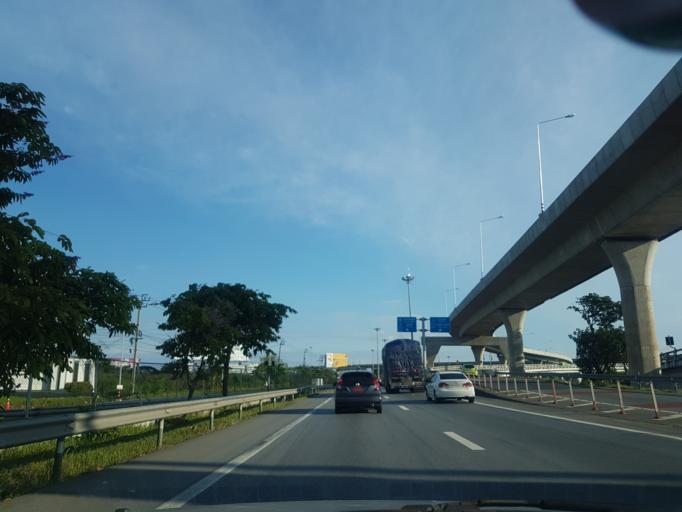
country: TH
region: Bangkok
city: Saphan Sung
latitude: 13.7347
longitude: 100.7045
